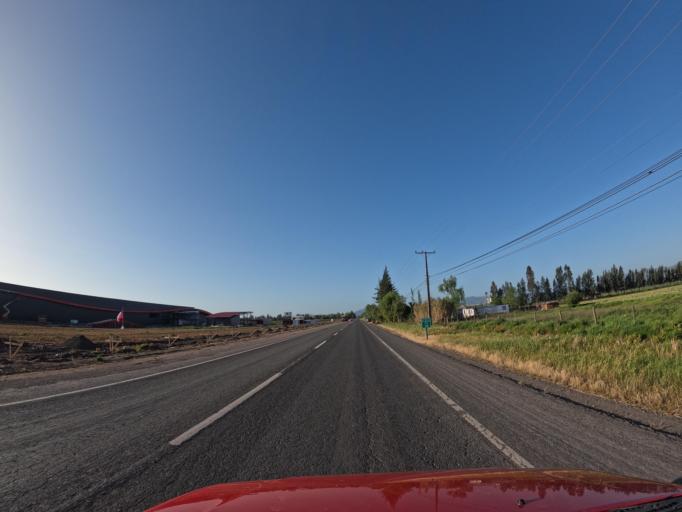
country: CL
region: O'Higgins
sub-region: Provincia de Colchagua
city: Santa Cruz
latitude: -34.5060
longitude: -71.3631
